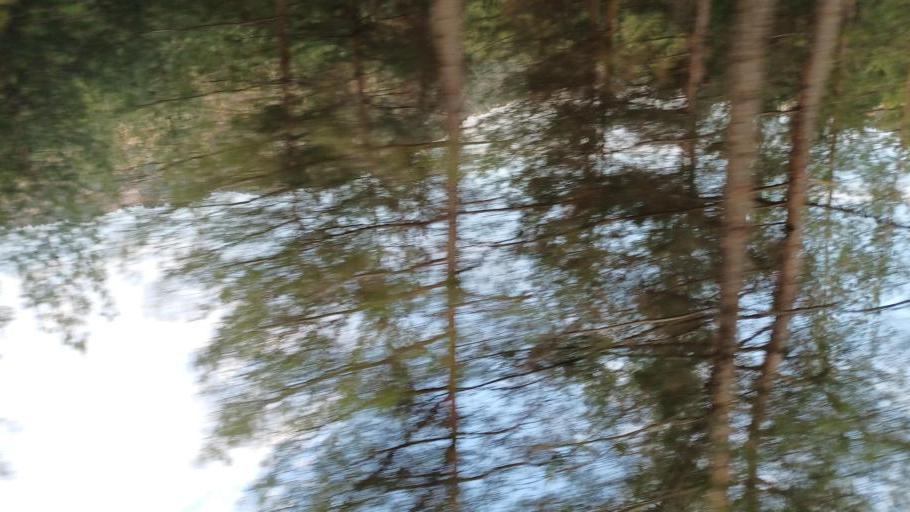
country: CY
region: Limassol
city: Kyperounta
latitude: 34.9378
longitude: 32.9322
